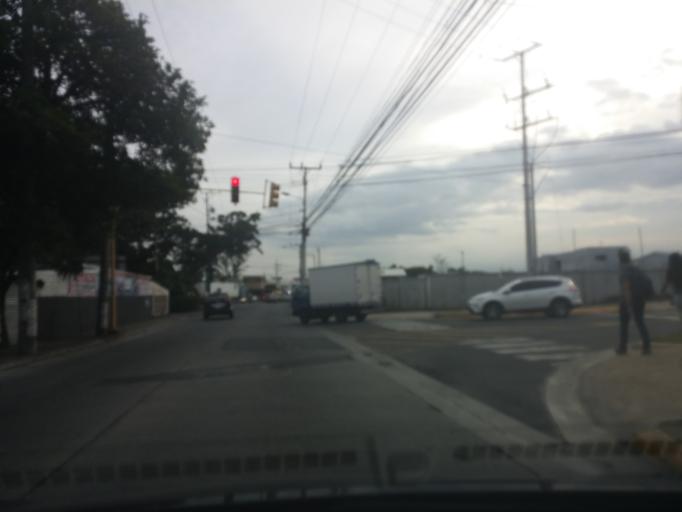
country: CR
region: Heredia
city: La Asuncion
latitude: 9.9831
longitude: -84.1580
